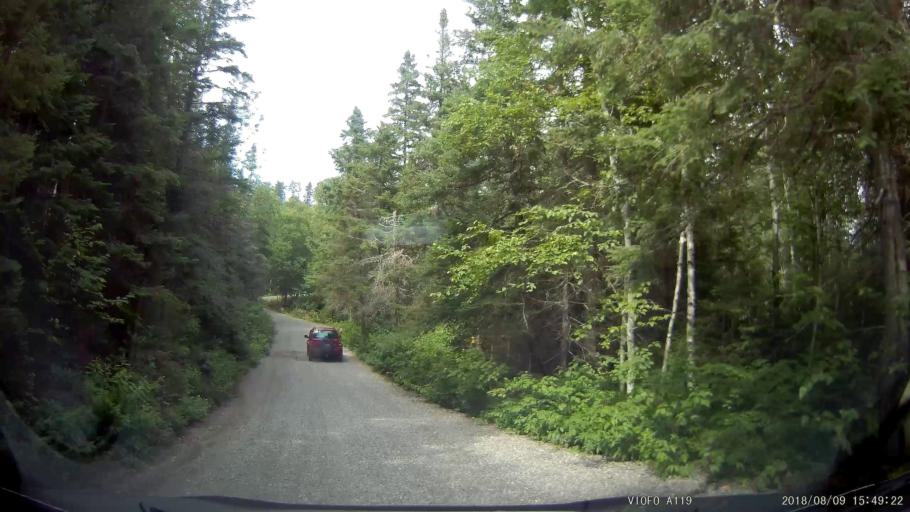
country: CA
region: Ontario
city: Rayside-Balfour
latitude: 46.5899
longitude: -81.5402
